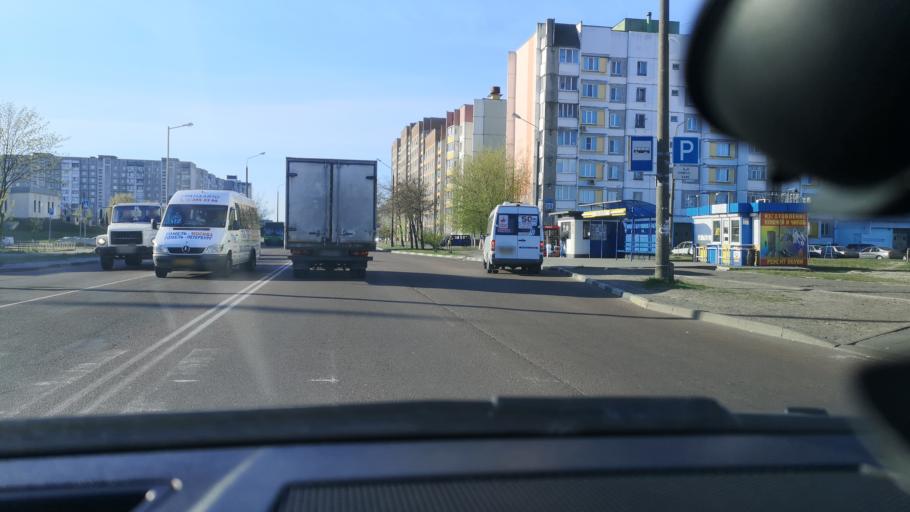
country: BY
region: Gomel
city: Gomel
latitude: 52.4051
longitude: 30.9197
